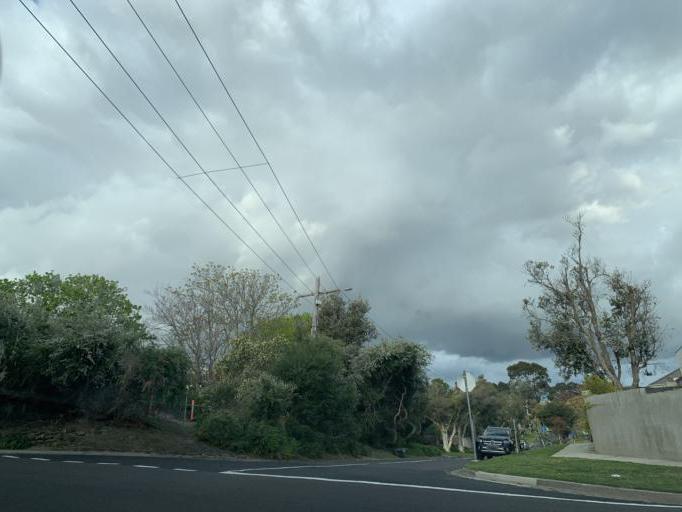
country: AU
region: Victoria
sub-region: Bayside
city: Black Rock
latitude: -37.9777
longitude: 145.0252
